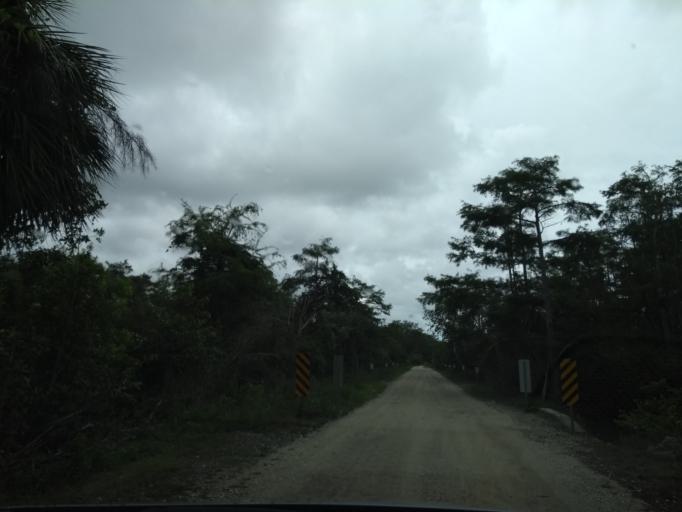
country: US
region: Florida
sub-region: Miami-Dade County
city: The Hammocks
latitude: 25.7465
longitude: -80.9513
